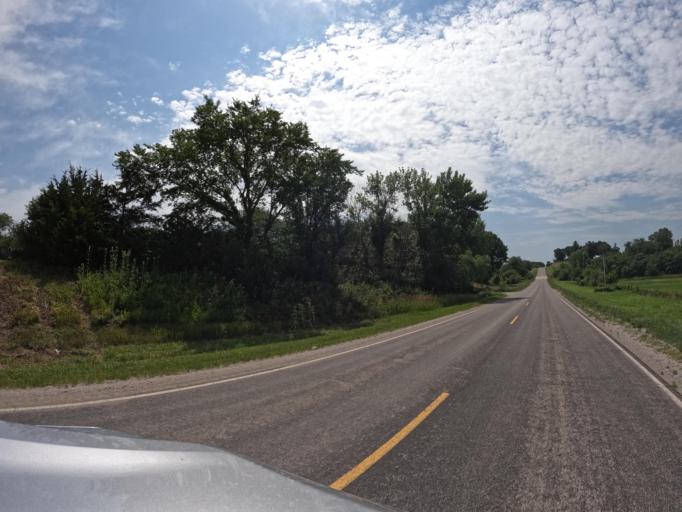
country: US
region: Iowa
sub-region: Appanoose County
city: Centerville
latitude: 40.7979
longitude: -92.9448
